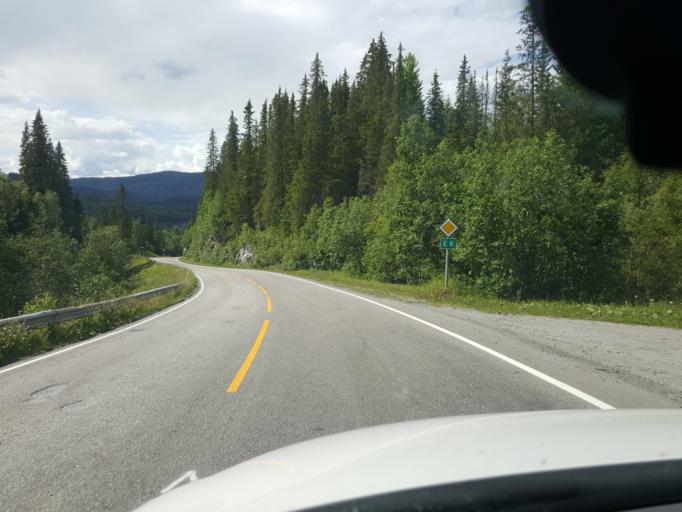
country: NO
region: Nordland
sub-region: Rana
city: Mo i Rana
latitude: 66.4076
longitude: 14.5158
